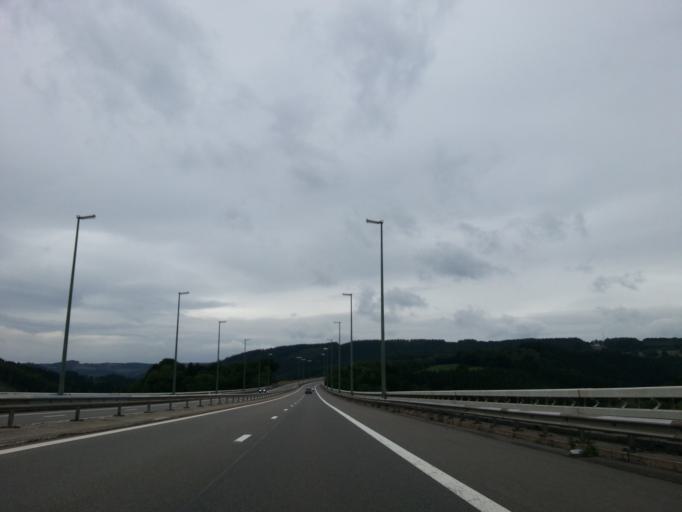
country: BE
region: Wallonia
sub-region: Province de Liege
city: Malmedy
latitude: 50.3856
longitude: 5.9931
